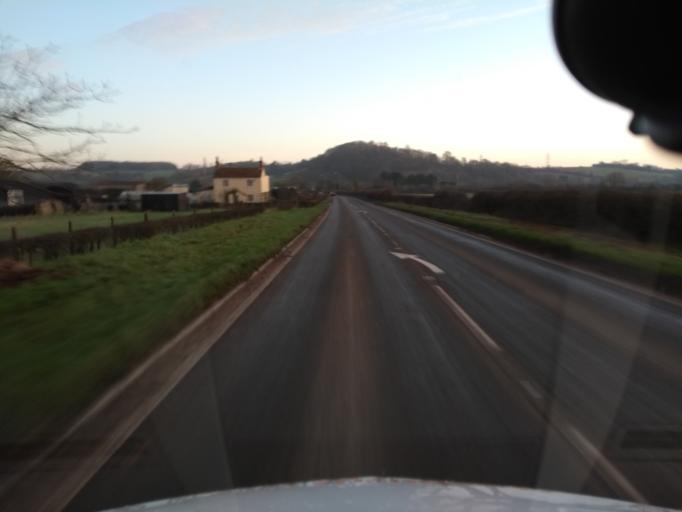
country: GB
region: England
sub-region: Somerset
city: Puriton
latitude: 51.1505
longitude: -2.9613
